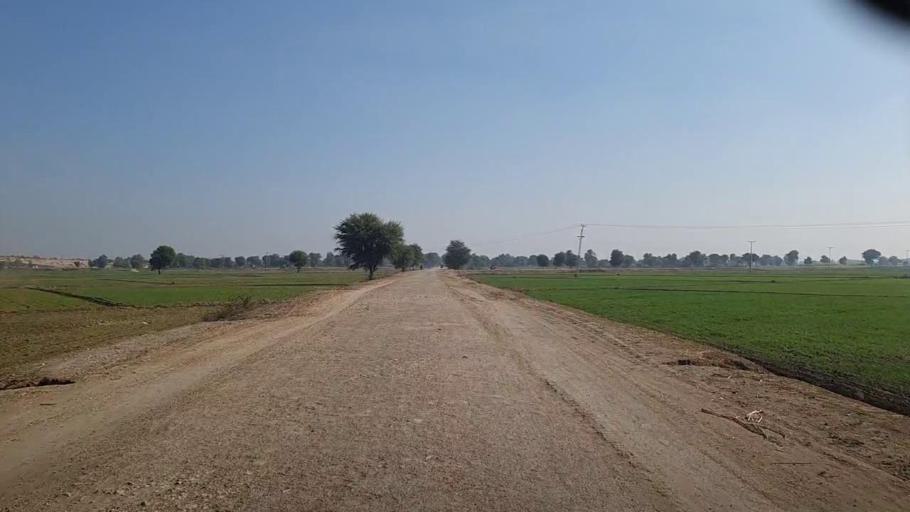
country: PK
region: Sindh
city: Darya Khan Marri
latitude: 26.6670
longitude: 68.3348
